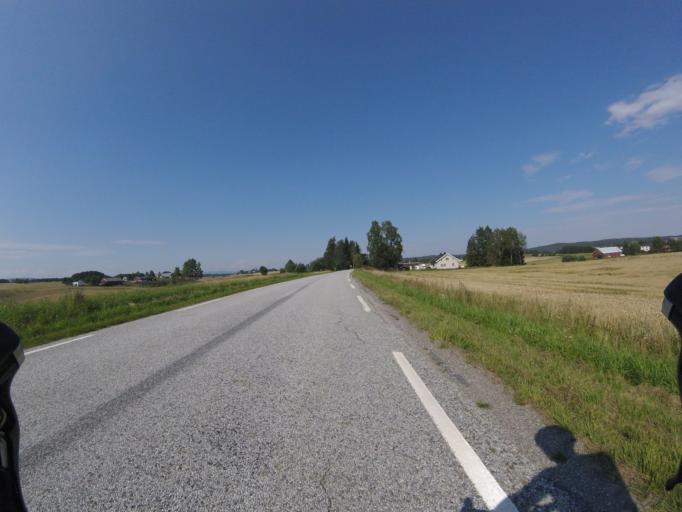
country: NO
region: Akershus
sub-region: Ullensaker
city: Klofta
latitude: 60.0889
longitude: 11.1620
